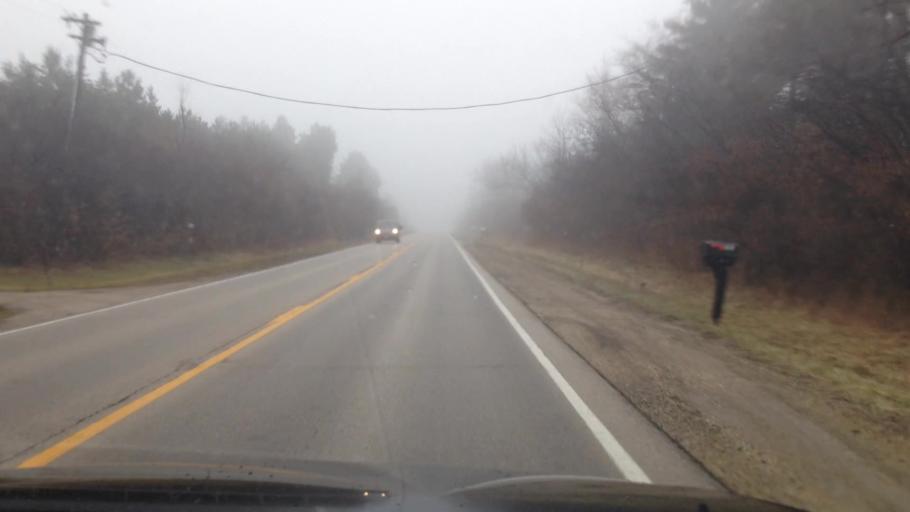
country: US
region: Illinois
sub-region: McHenry County
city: Woodstock
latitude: 42.3807
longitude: -88.4432
